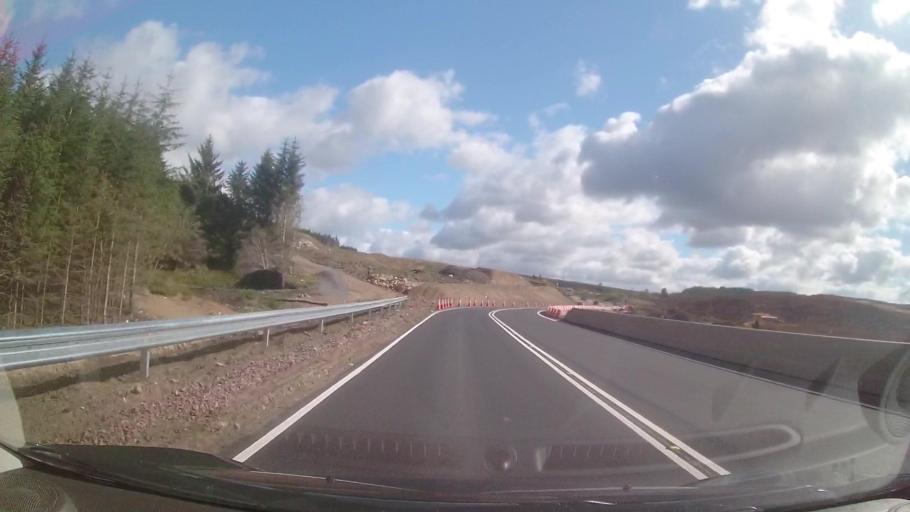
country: GB
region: Wales
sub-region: Rhondda Cynon Taf
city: Aberdare
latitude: 51.7537
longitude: -3.4543
